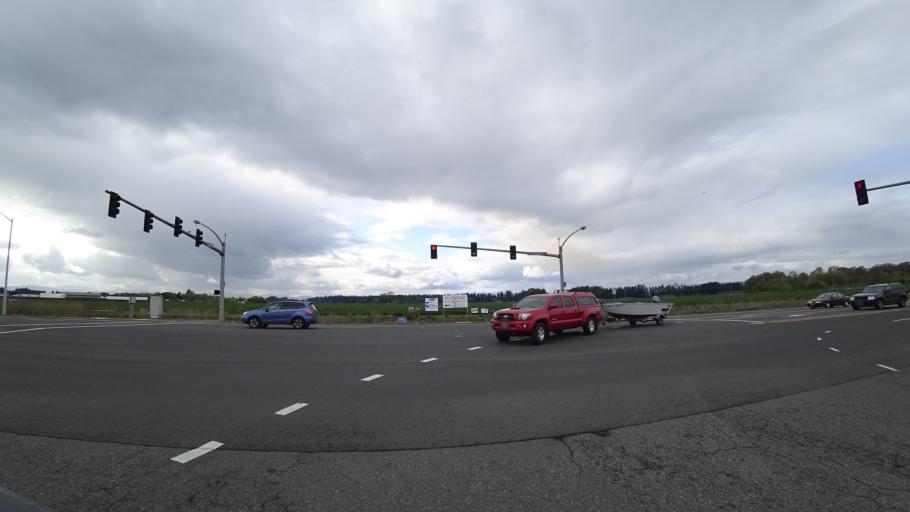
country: US
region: Oregon
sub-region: Washington County
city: Hillsboro
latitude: 45.5517
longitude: -122.9639
